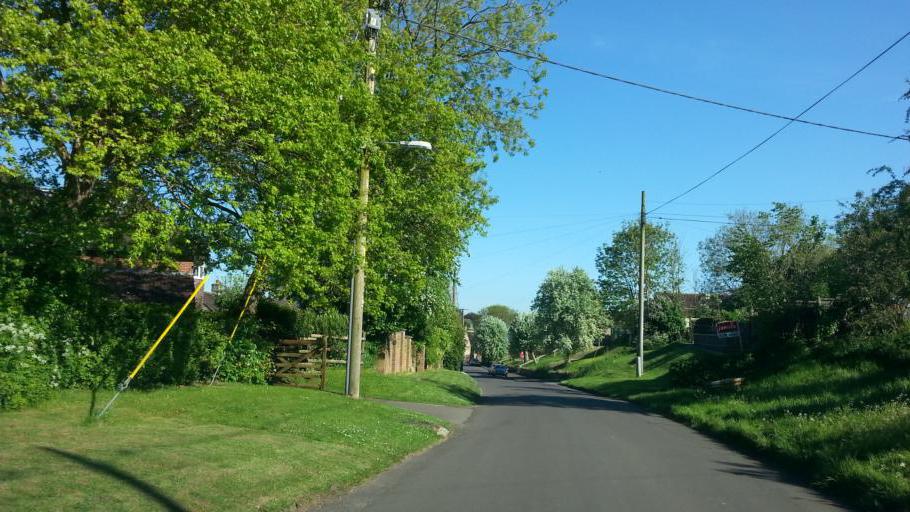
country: GB
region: England
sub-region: Somerset
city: Milborne Port
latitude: 50.9706
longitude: -2.4667
